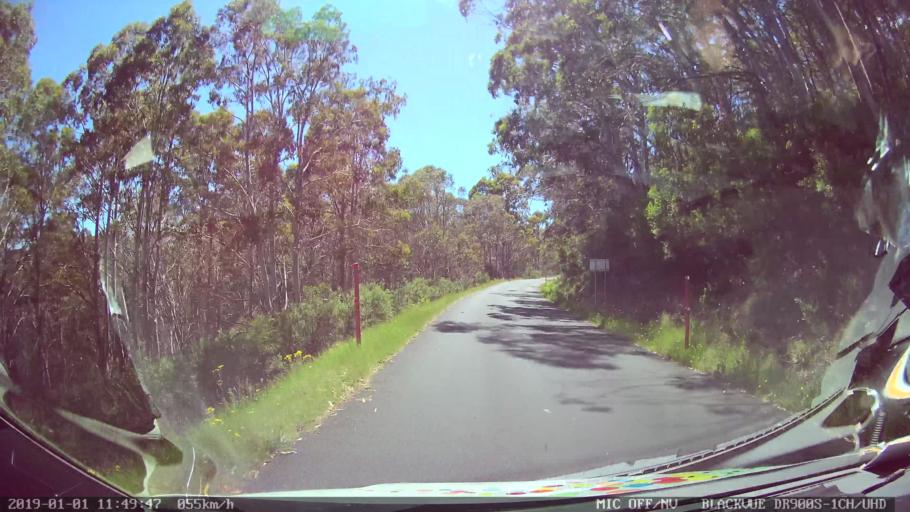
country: AU
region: New South Wales
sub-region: Snowy River
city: Jindabyne
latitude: -35.8915
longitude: 148.4150
